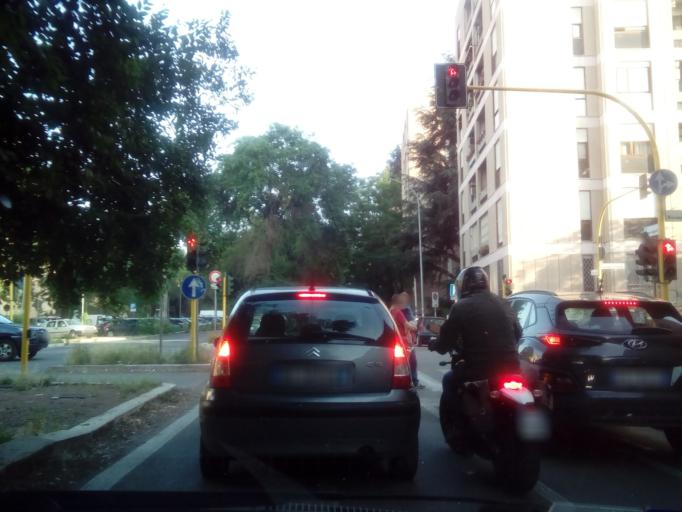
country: IT
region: Latium
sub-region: Citta metropolitana di Roma Capitale
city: Rome
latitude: 41.8593
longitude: 12.5703
